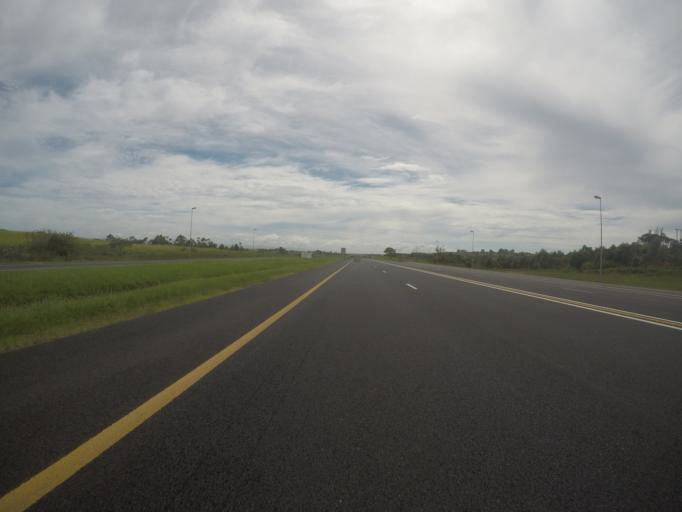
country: ZA
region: KwaZulu-Natal
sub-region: iLembe District Municipality
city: Mandeni
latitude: -29.0819
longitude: 31.6115
